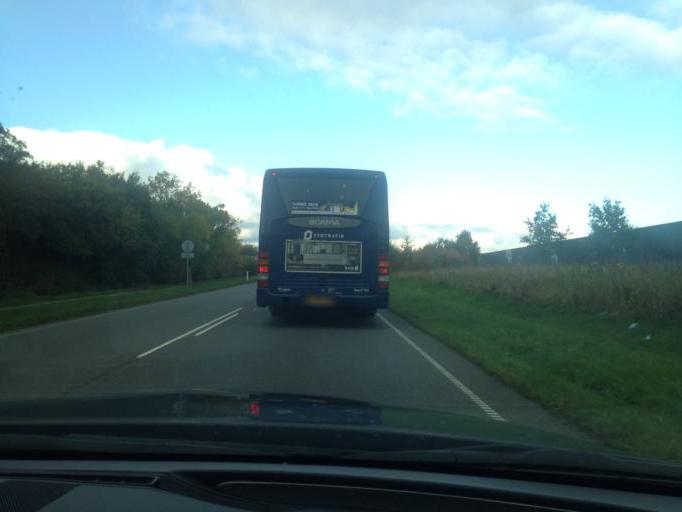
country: DK
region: South Denmark
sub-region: Kolding Kommune
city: Kolding
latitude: 55.5460
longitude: 9.4779
